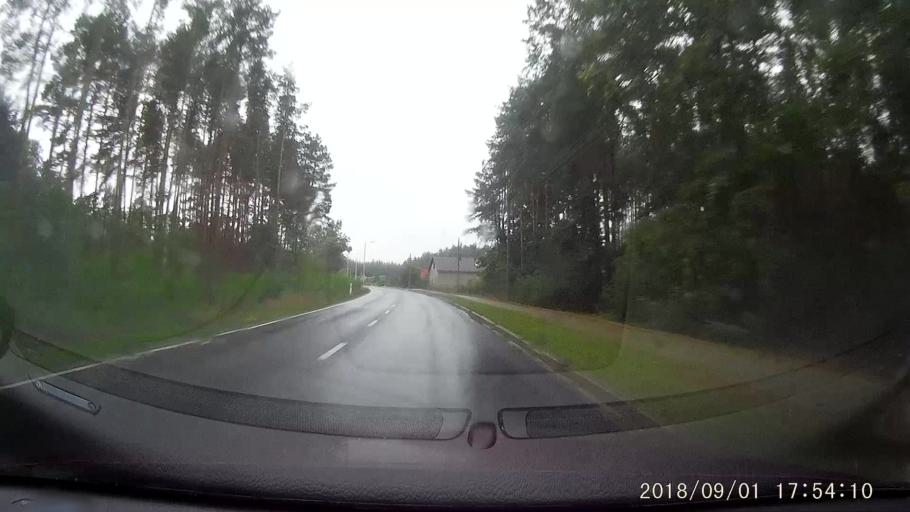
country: PL
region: Lubusz
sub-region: Powiat zaganski
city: Ilowa
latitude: 51.4714
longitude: 15.1995
